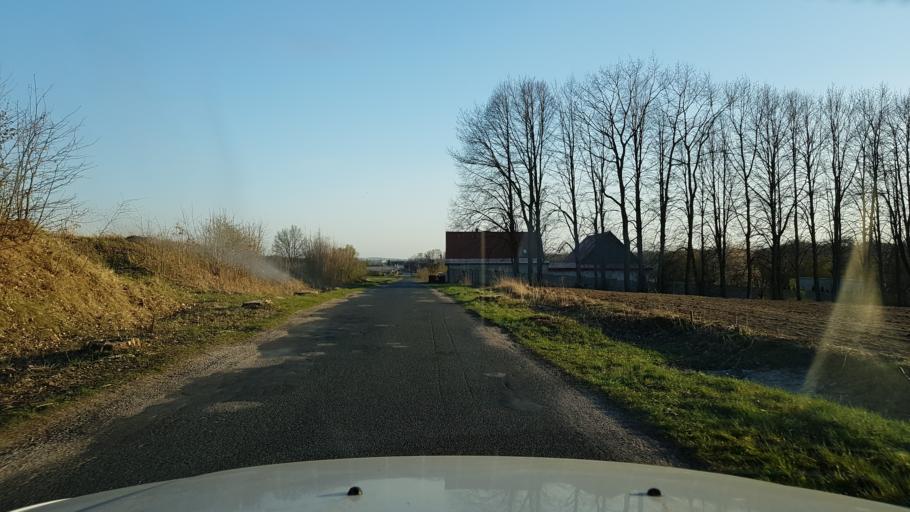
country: PL
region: West Pomeranian Voivodeship
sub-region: Powiat bialogardzki
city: Bialogard
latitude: 54.0317
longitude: 15.9897
